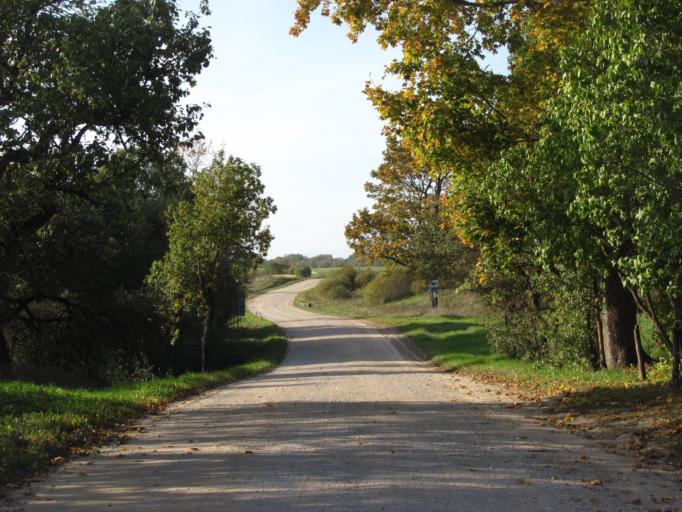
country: LV
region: Akniste
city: Akniste
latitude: 55.9127
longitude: 25.8702
